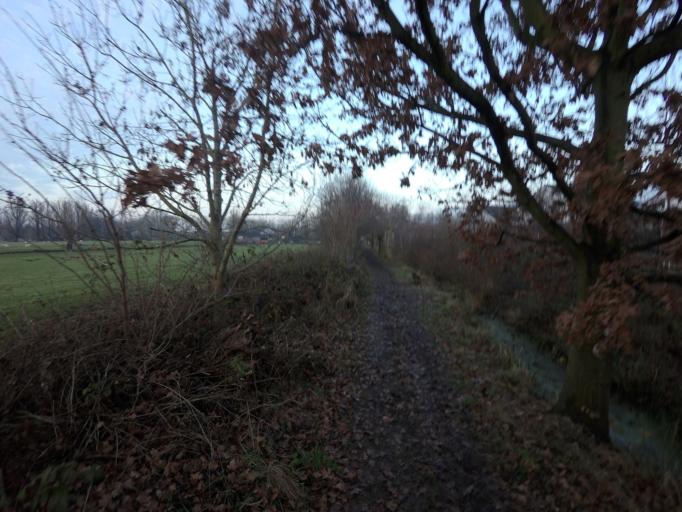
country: NL
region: Utrecht
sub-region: Gemeente Montfoort
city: Montfoort
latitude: 52.0883
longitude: 4.9530
